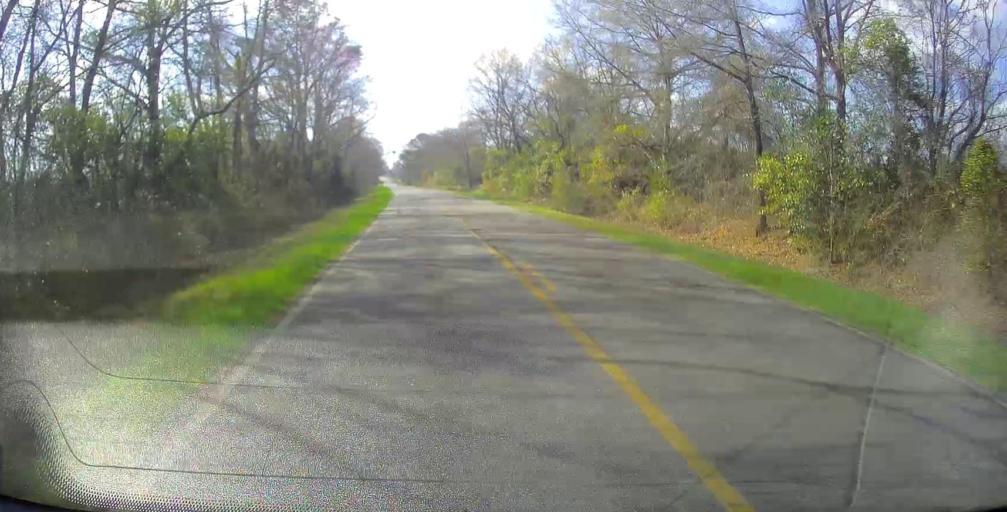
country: US
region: Georgia
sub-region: Wilkinson County
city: Irwinton
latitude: 32.6357
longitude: -83.1260
